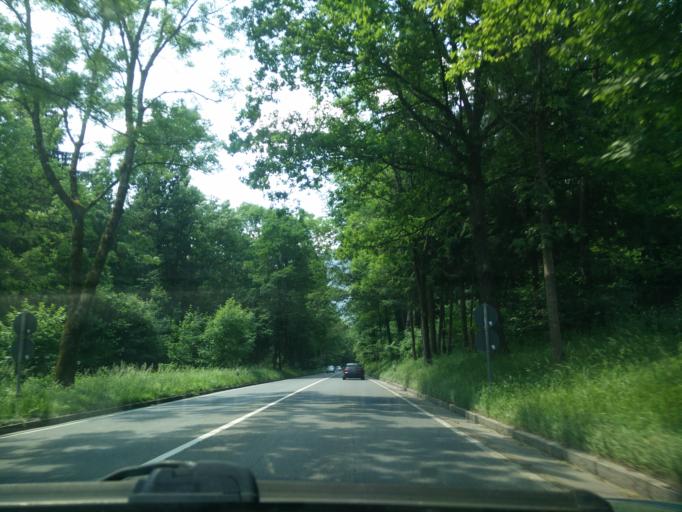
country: DE
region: Bavaria
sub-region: Upper Bavaria
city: Piding
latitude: 47.7763
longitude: 12.9271
